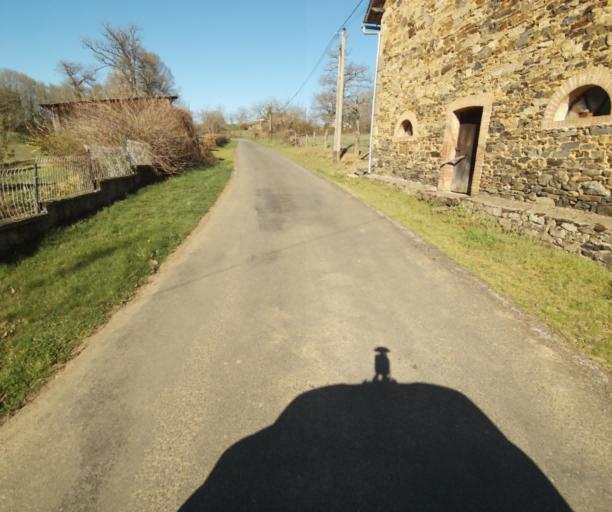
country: FR
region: Limousin
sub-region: Departement de la Correze
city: Seilhac
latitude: 45.3814
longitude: 1.7660
